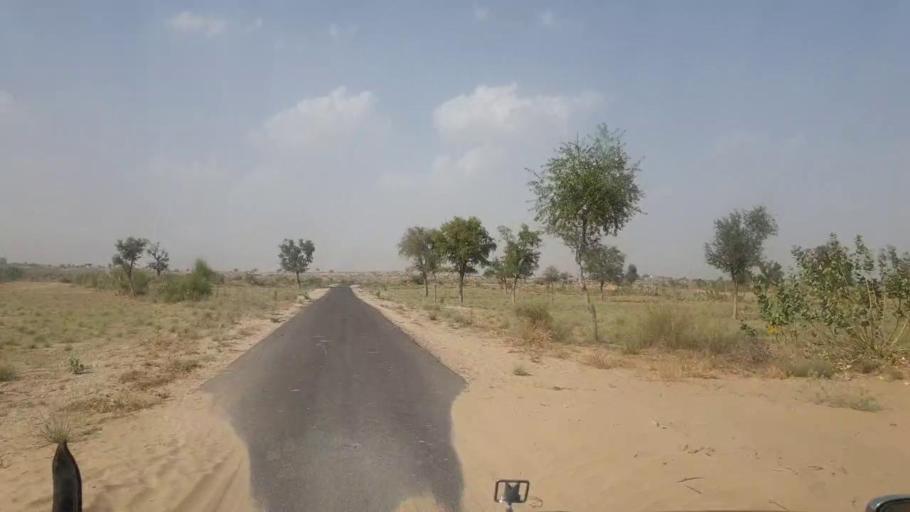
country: PK
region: Sindh
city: Islamkot
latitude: 25.2016
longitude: 70.2837
